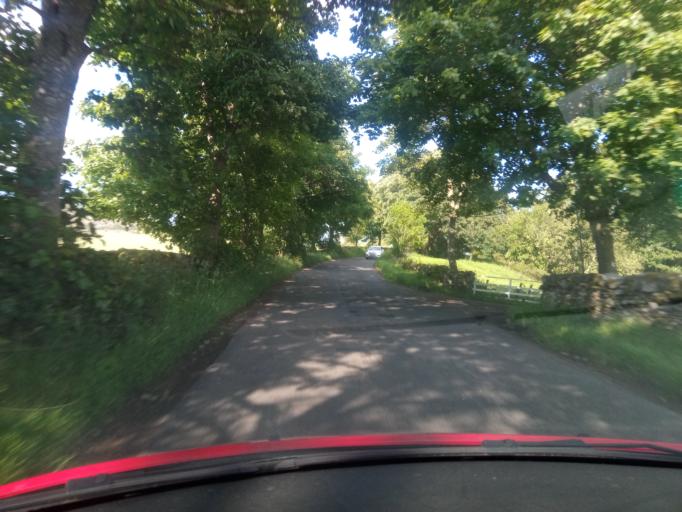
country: GB
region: Scotland
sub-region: The Scottish Borders
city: Innerleithen
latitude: 55.5048
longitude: -2.9815
